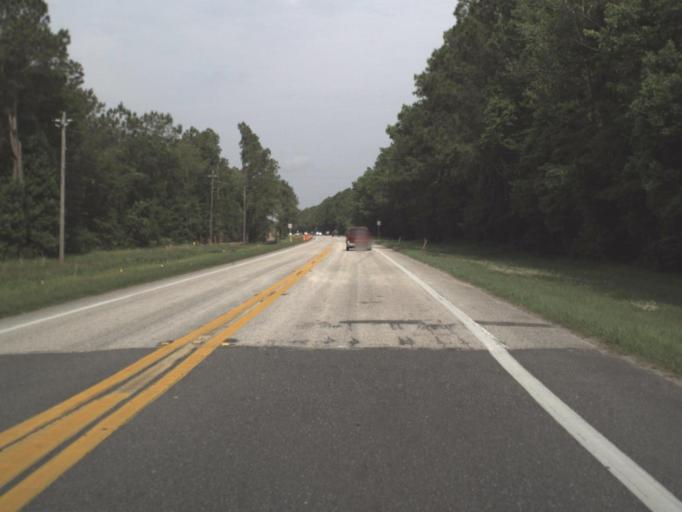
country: US
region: Florida
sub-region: Saint Johns County
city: Saint Augustine
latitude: 29.9603
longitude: -81.4708
